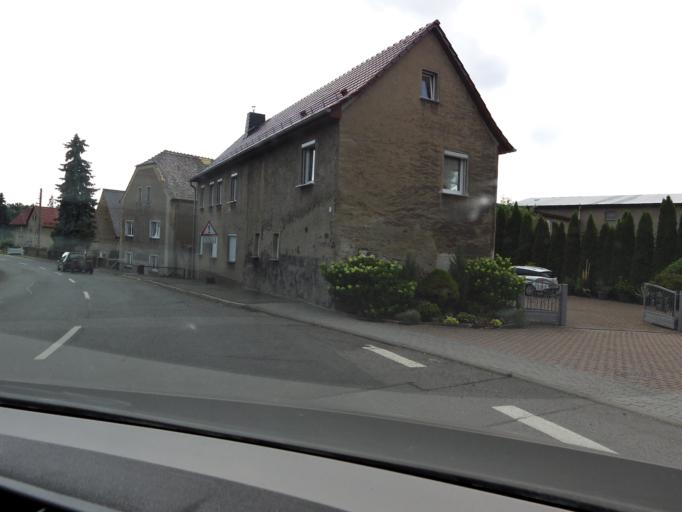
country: DE
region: Saxony
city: Grossbardau
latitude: 51.2362
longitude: 12.6603
